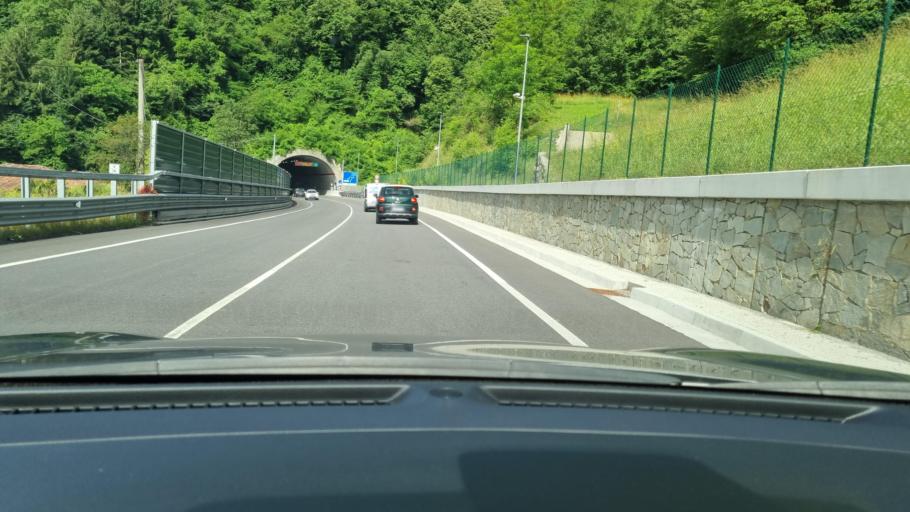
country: IT
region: Lombardy
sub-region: Provincia di Bergamo
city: Zogno
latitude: 45.7942
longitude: 9.6456
